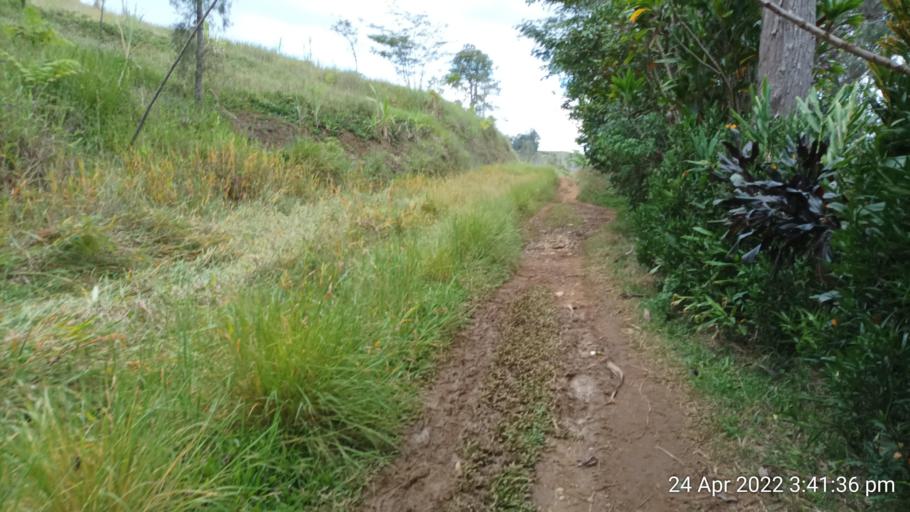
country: PG
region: Jiwaka
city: Minj
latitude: -5.8939
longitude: 144.8216
